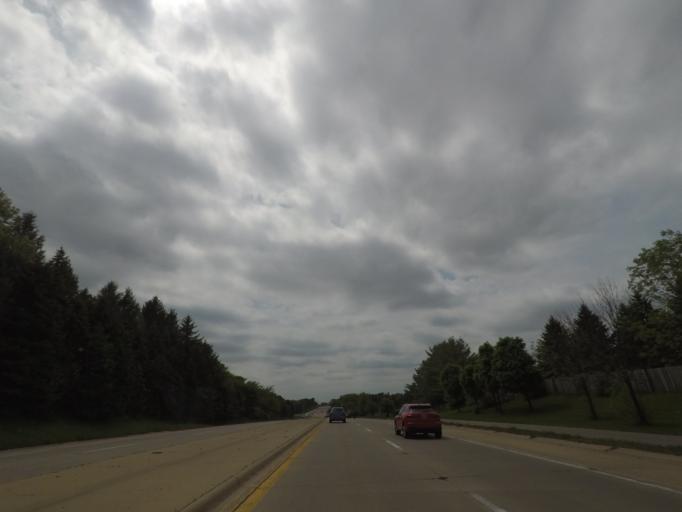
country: US
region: Illinois
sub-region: Winnebago County
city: Cherry Valley
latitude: 42.2868
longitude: -88.9805
